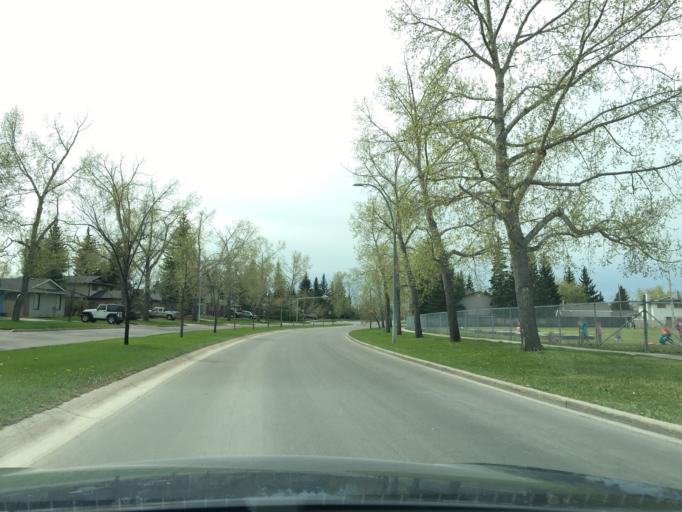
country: CA
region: Alberta
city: Calgary
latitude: 50.9452
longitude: -114.0601
